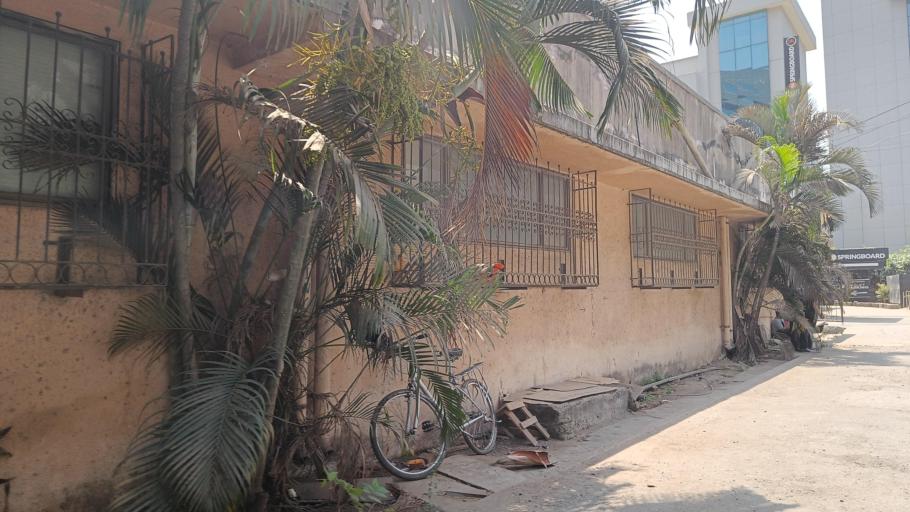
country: IN
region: Maharashtra
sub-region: Mumbai Suburban
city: Mumbai
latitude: 19.0733
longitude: 72.8700
